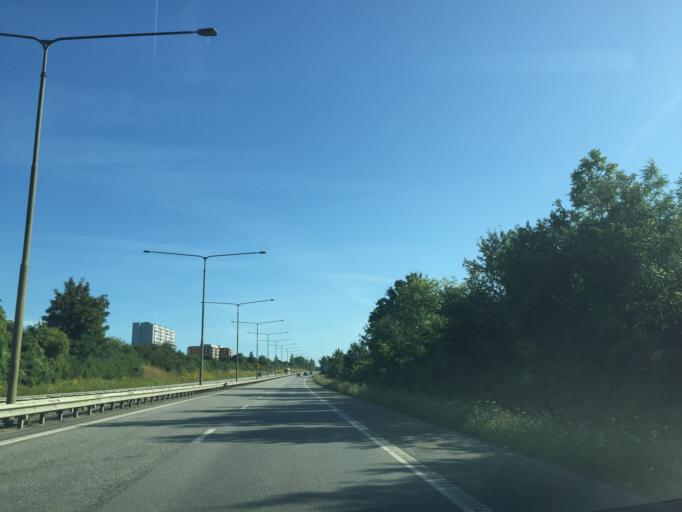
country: SE
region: Skane
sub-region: Malmo
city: Malmoe
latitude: 55.5744
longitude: 13.0048
